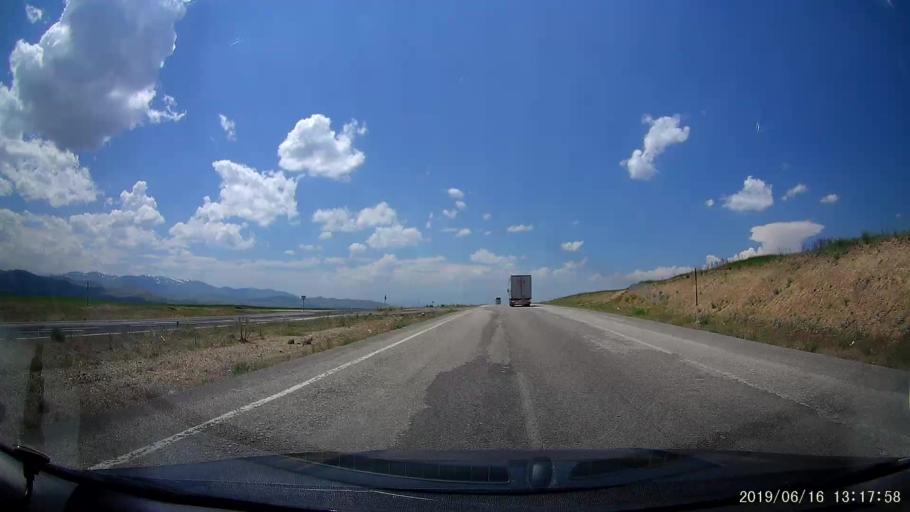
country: TR
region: Agri
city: Taslicay
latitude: 39.6289
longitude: 43.4408
